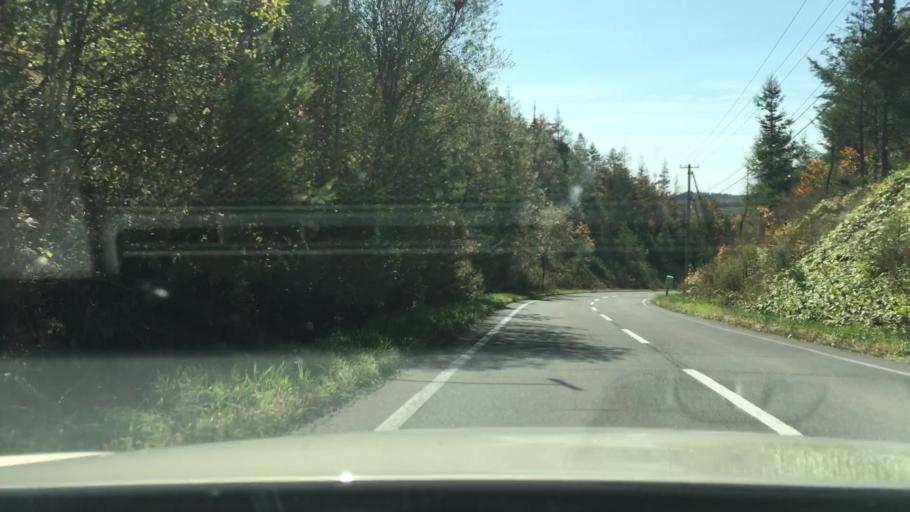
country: JP
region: Hokkaido
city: Kitami
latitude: 43.5967
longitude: 143.6820
